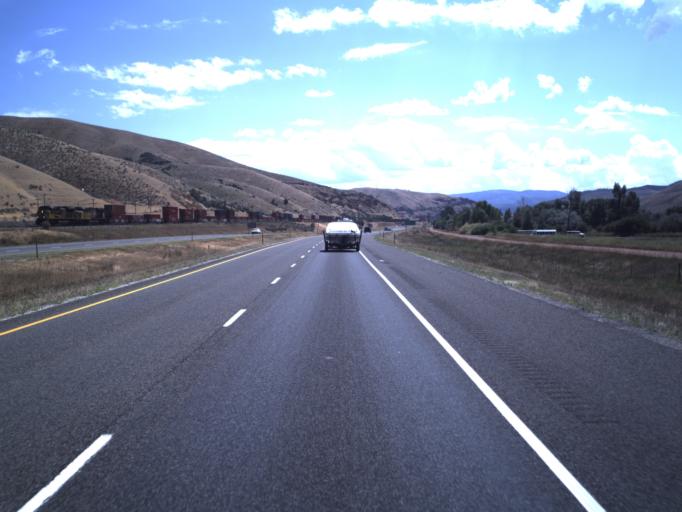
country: US
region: Utah
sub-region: Summit County
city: Coalville
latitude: 41.0093
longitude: -111.4807
